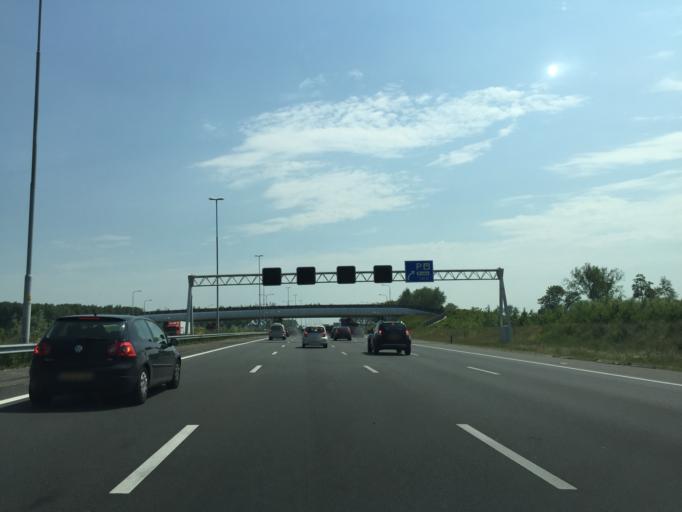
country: NL
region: Gelderland
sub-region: Gemeente Culemborg
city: Culemborg
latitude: 51.9186
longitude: 5.1746
